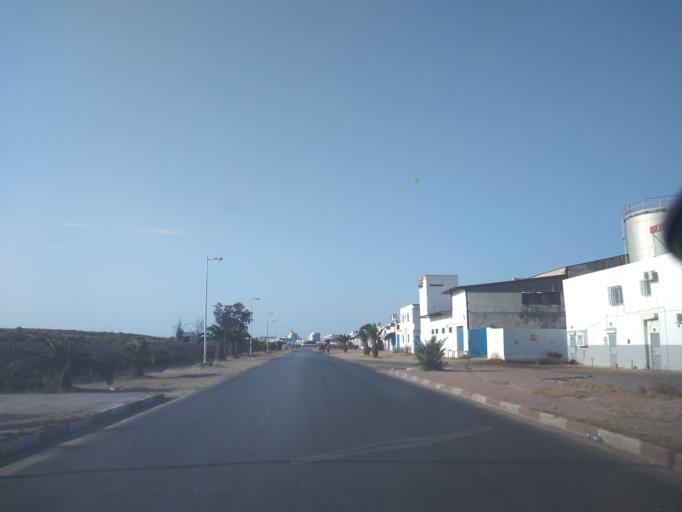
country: TN
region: Safaqis
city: Sfax
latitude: 34.7175
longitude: 10.7609
